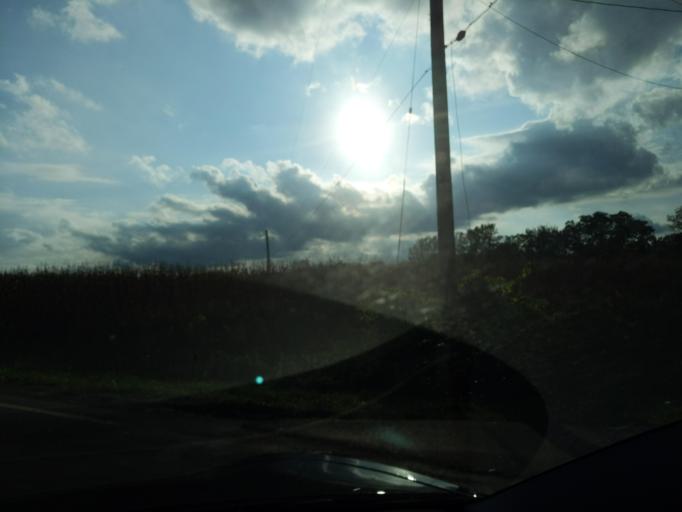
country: US
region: Michigan
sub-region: Ingham County
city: Leslie
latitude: 42.3713
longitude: -84.4629
